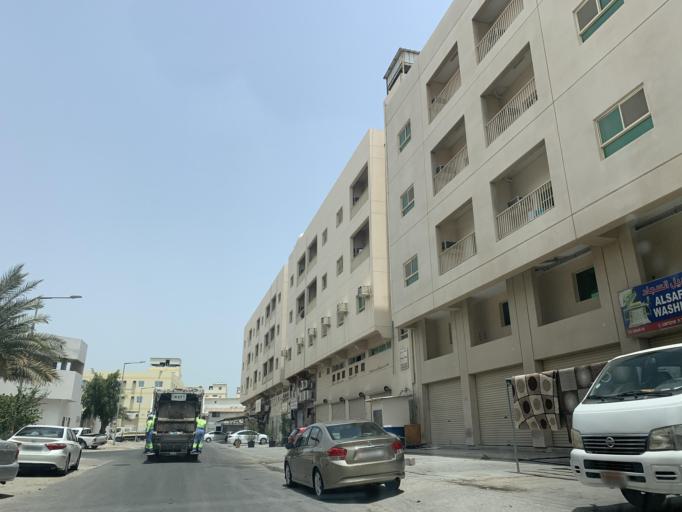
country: BH
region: Northern
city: Ar Rifa'
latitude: 26.1356
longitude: 50.5866
